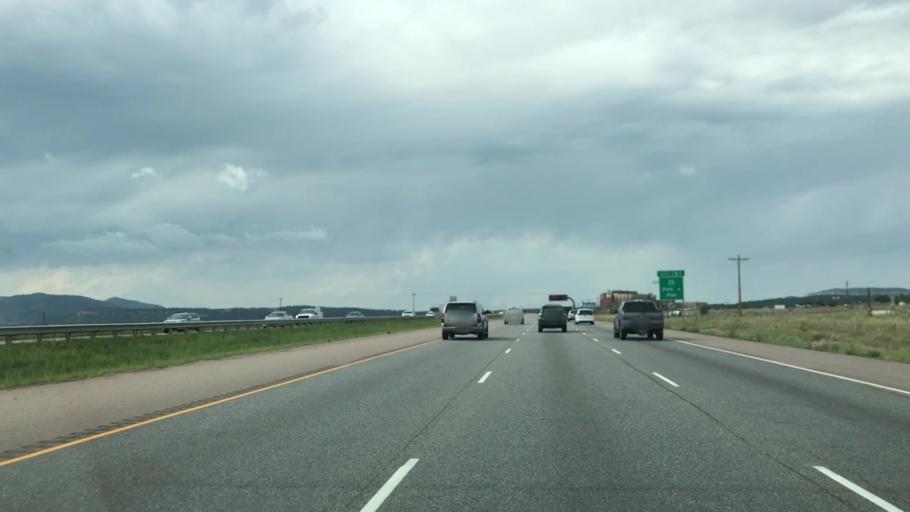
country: US
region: Colorado
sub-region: El Paso County
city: Monument
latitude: 39.0754
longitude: -104.8586
